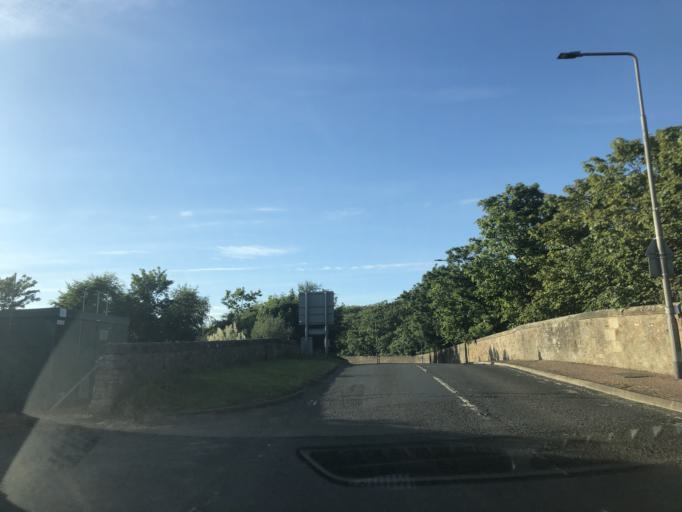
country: GB
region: Scotland
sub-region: Fife
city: Saint Monance
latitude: 56.1931
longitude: -2.8221
